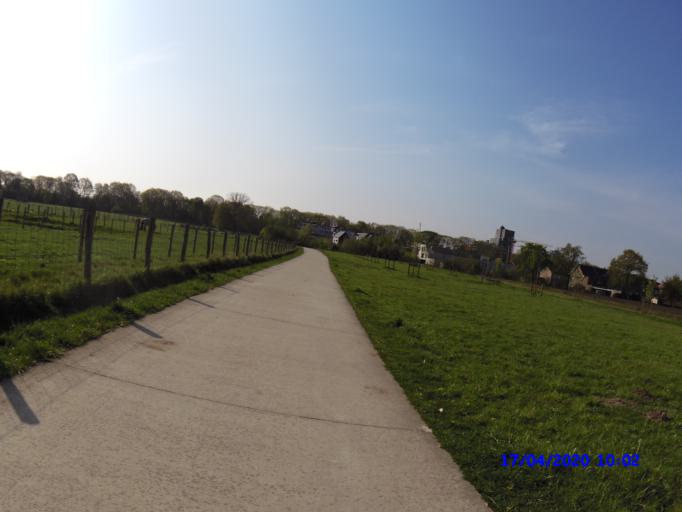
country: BE
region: Flanders
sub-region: Provincie Antwerpen
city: Turnhout
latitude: 51.3325
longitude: 4.9358
